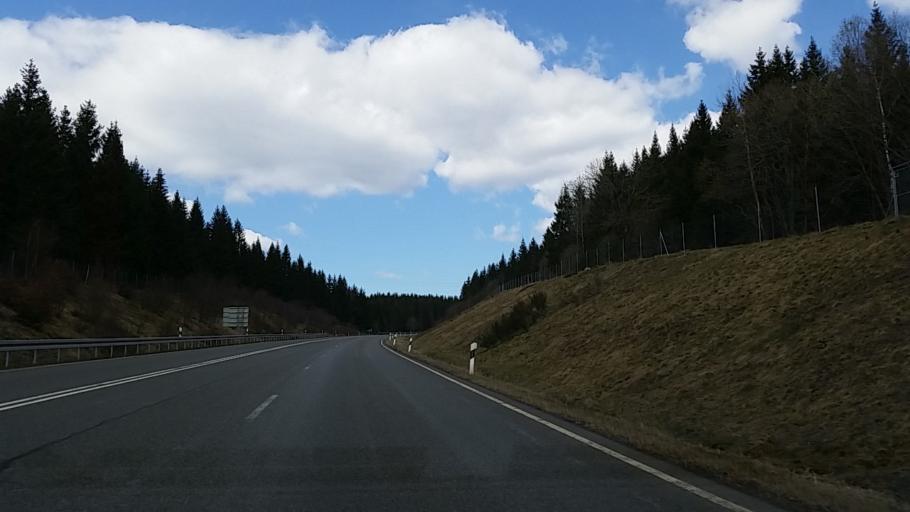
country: DE
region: Lower Saxony
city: Braunlage
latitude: 51.7203
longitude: 10.5931
